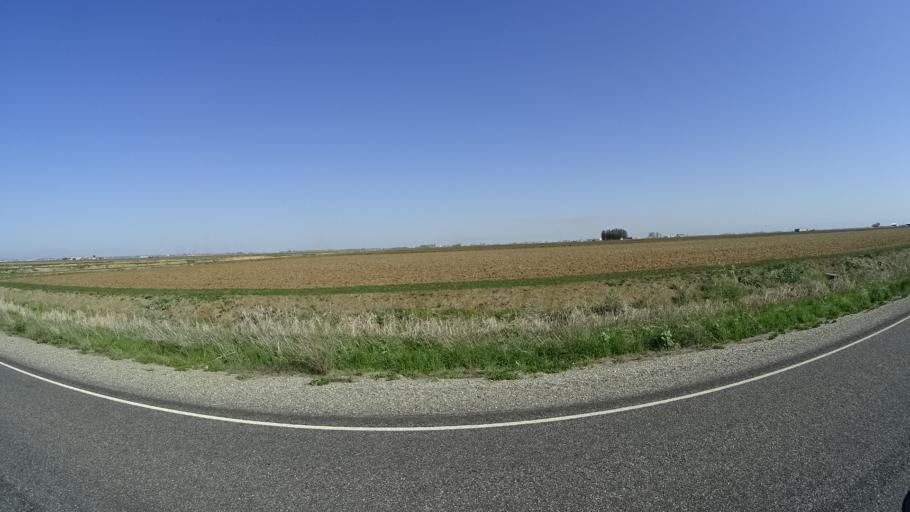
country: US
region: California
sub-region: Glenn County
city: Willows
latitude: 39.4656
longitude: -122.1450
